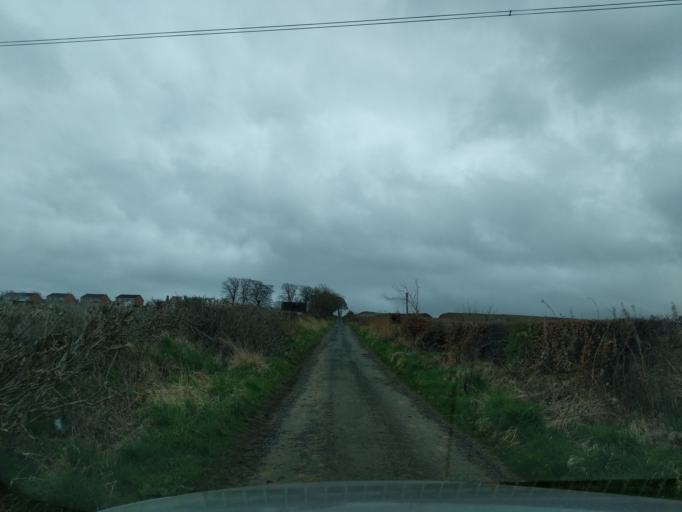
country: GB
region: Scotland
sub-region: Edinburgh
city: Balerno
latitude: 55.8953
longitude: -3.3391
